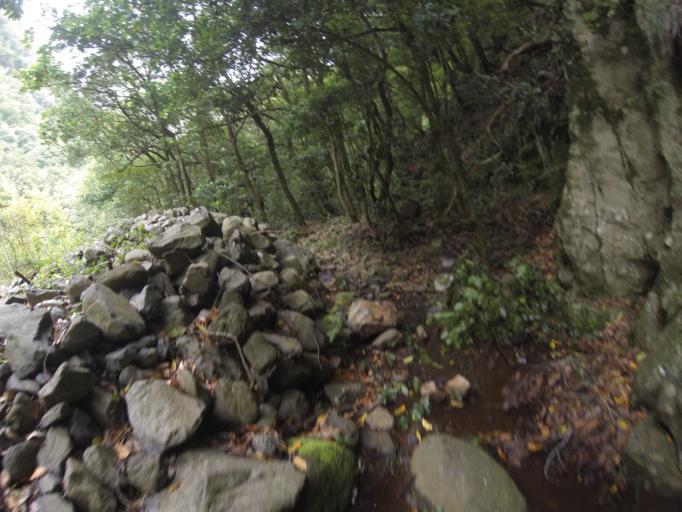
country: PT
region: Madeira
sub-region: Sao Vicente
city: Sao Vicente
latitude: 32.7916
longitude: -17.1140
